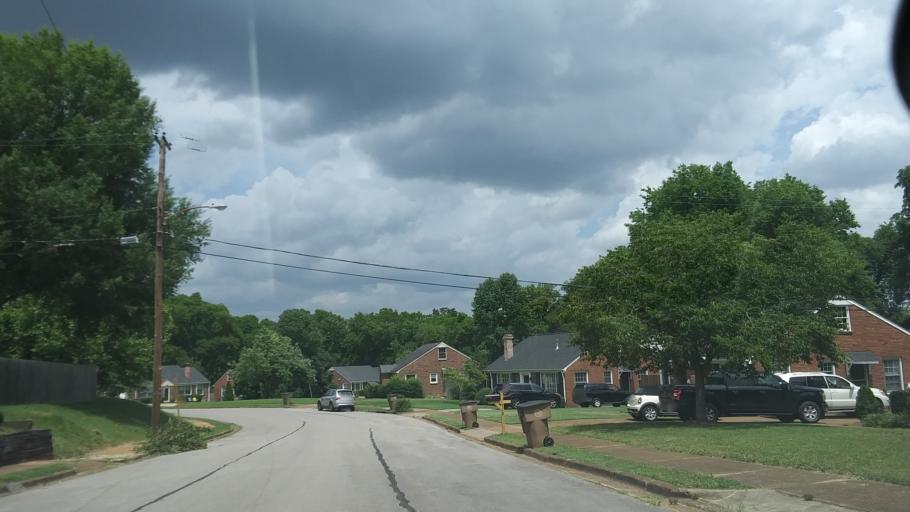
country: US
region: Tennessee
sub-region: Davidson County
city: Belle Meade
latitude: 36.1360
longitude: -86.8602
